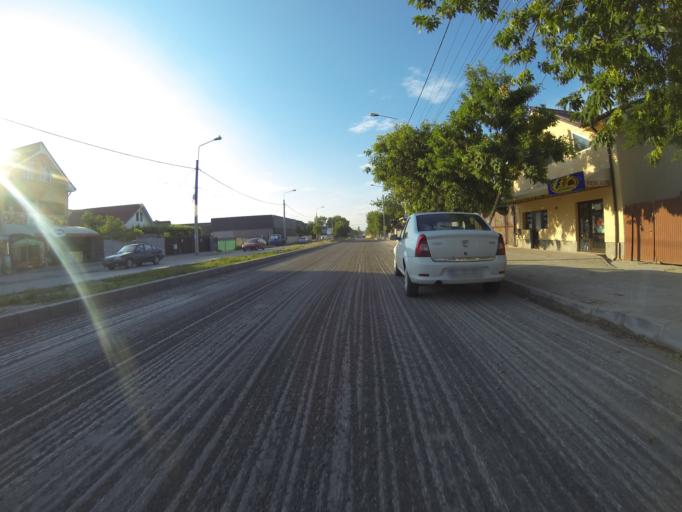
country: RO
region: Dolj
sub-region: Municipiul Craiova
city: Popoveni
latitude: 44.2881
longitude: 23.7996
